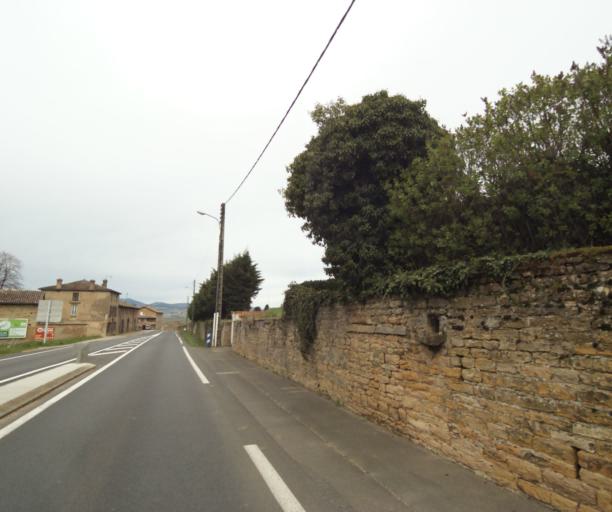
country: FR
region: Bourgogne
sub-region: Departement de Saone-et-Loire
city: Charnay-les-Macon
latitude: 46.3133
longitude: 4.7843
